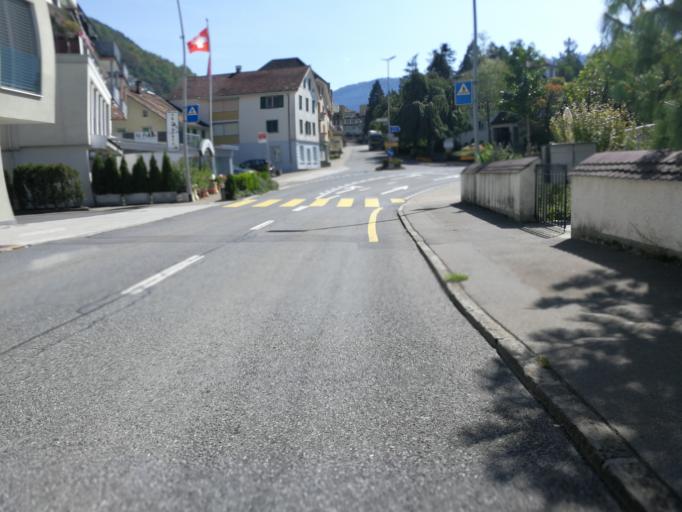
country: CH
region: Schwyz
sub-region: Bezirk Gersau
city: Gersau
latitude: 46.9927
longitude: 8.5229
